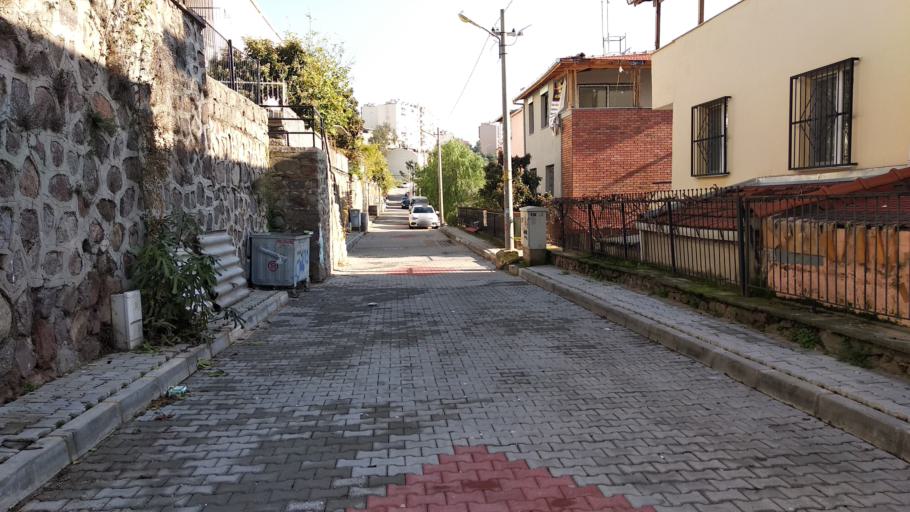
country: TR
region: Izmir
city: Karsiyaka
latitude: 38.4961
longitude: 27.0821
